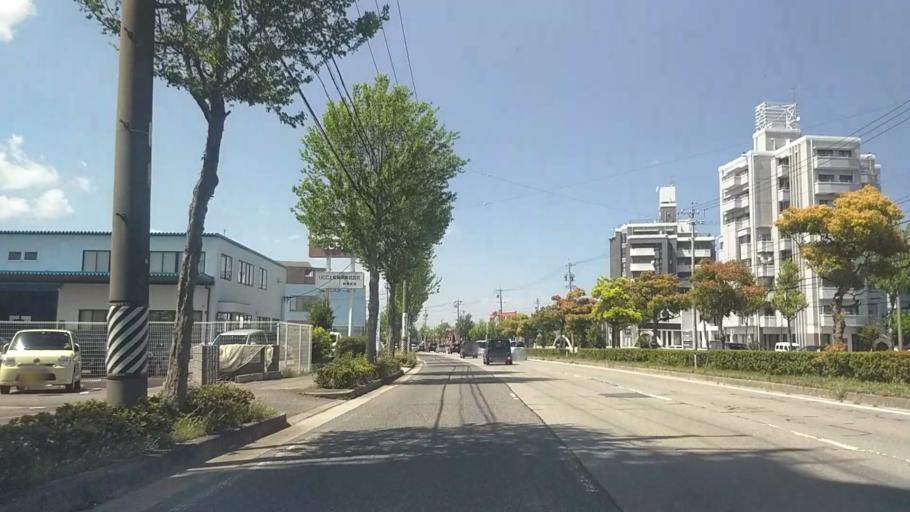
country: JP
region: Aichi
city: Okazaki
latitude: 34.9586
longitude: 137.1892
